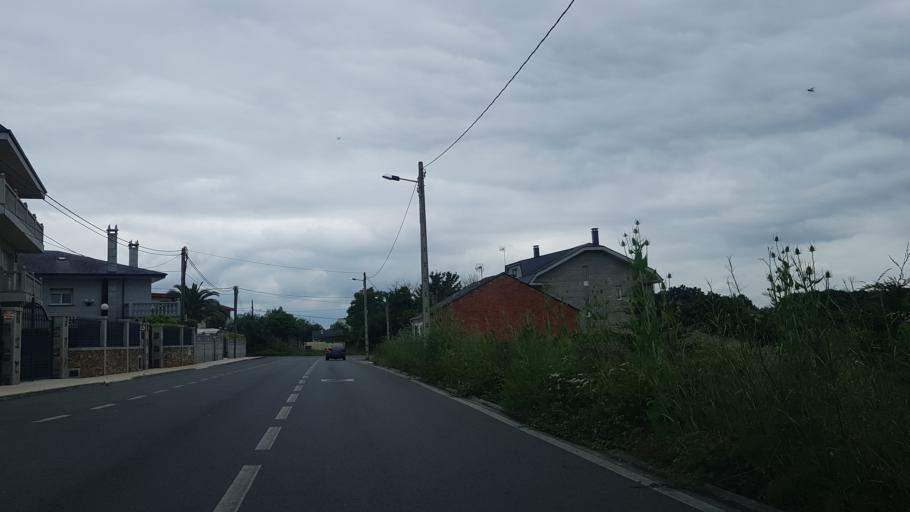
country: ES
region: Galicia
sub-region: Provincia de Lugo
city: Lugo
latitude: 43.0285
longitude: -7.5517
